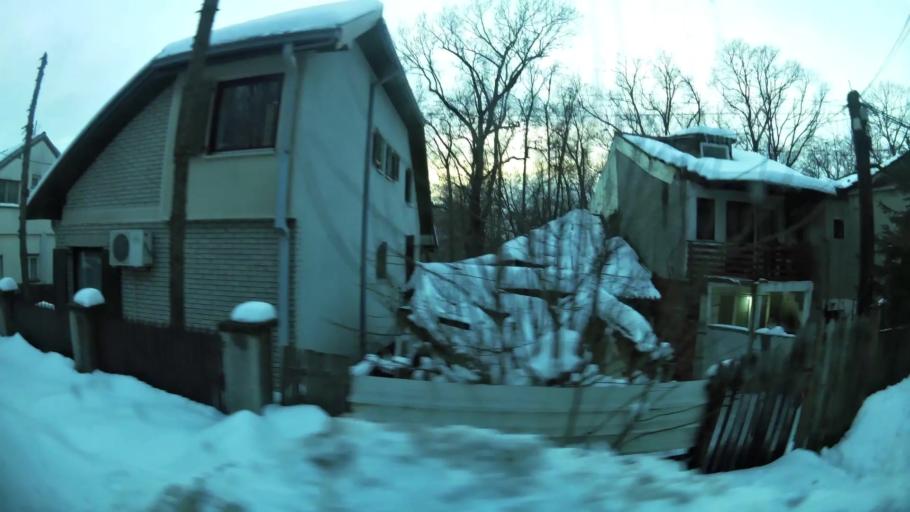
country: RS
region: Central Serbia
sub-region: Belgrade
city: Palilula
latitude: 44.8006
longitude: 20.5066
